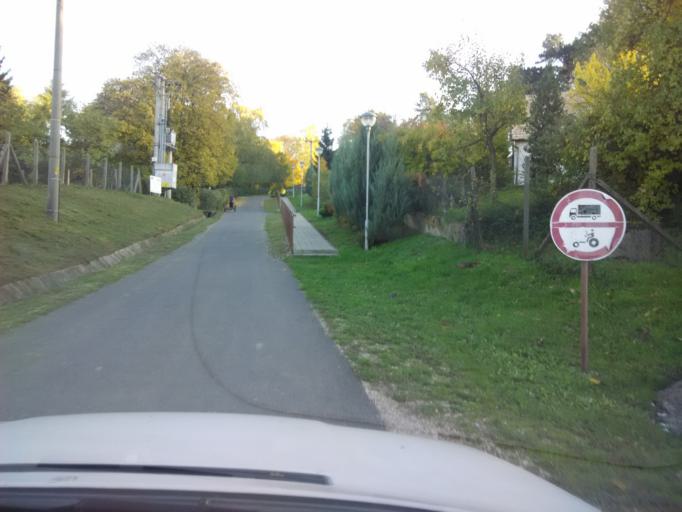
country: SK
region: Nitriansky
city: Svodin
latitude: 48.0404
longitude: 18.4710
